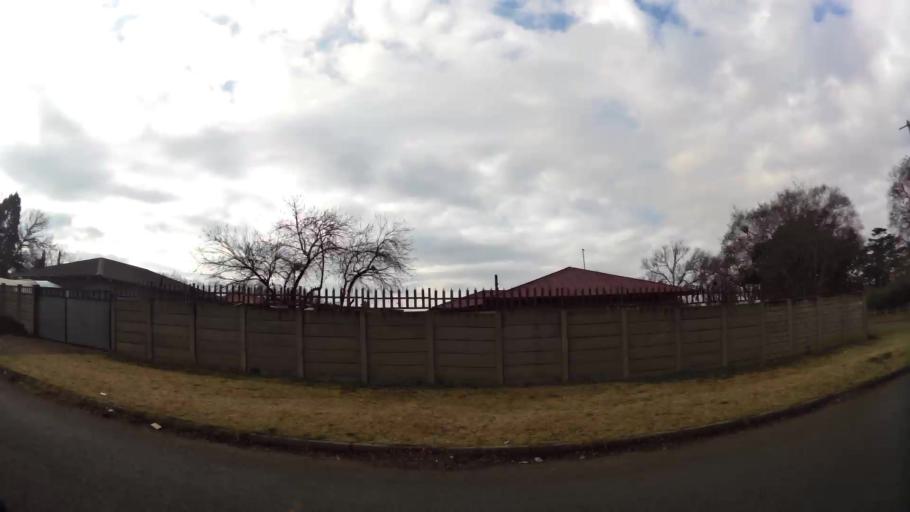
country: ZA
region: Gauteng
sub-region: Sedibeng District Municipality
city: Vanderbijlpark
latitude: -26.6931
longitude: 27.8192
